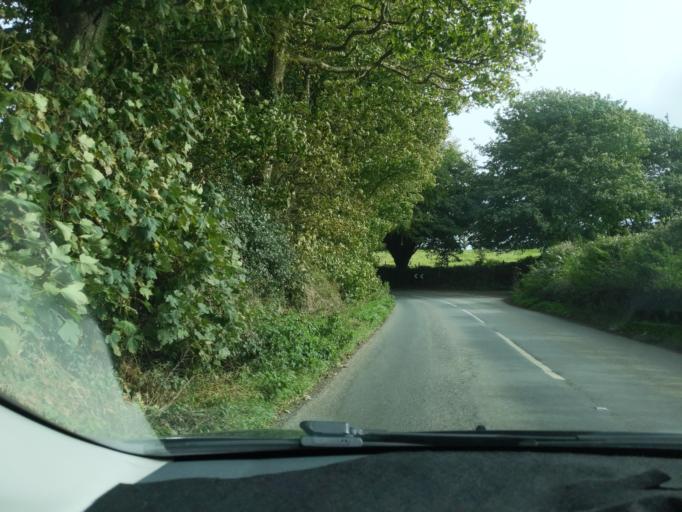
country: GB
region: England
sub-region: Cornwall
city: Mevagissey
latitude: 50.2470
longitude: -4.8145
